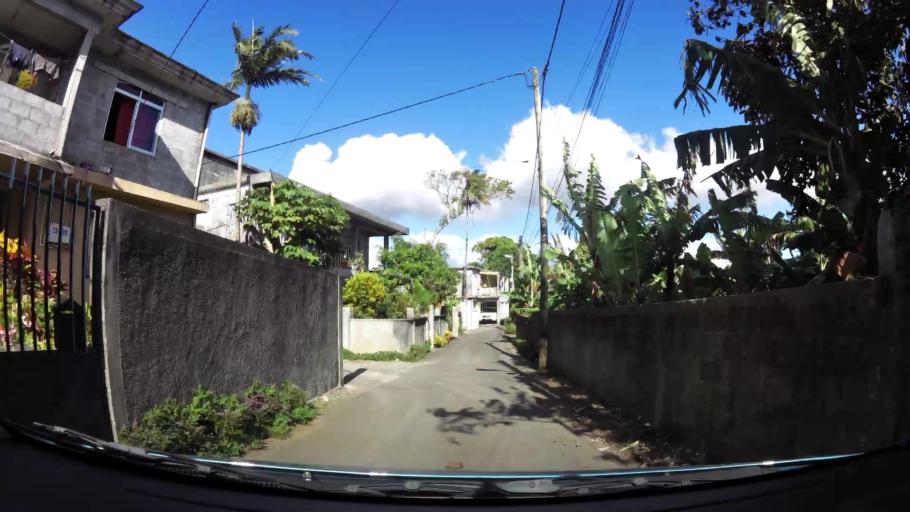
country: MU
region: Plaines Wilhems
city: Curepipe
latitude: -20.2964
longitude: 57.5169
